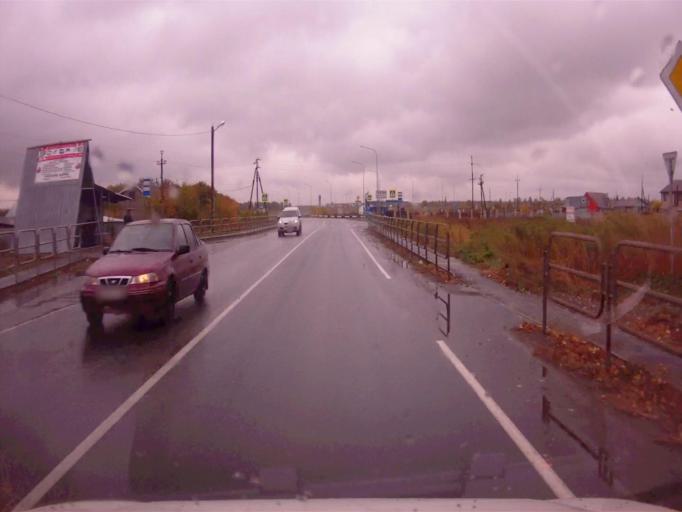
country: RU
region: Chelyabinsk
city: Roshchino
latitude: 55.3685
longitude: 61.1860
